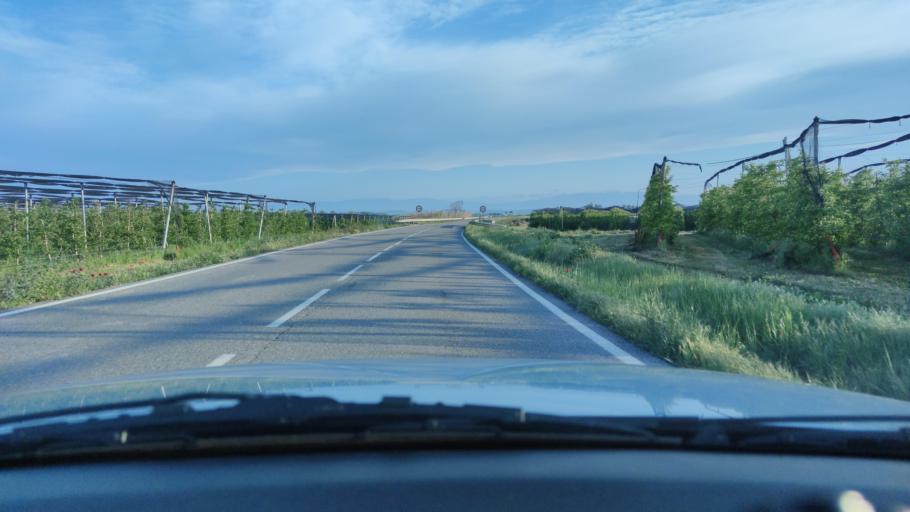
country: ES
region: Catalonia
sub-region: Provincia de Lleida
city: Ivars d'Urgell
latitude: 41.7011
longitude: 0.9823
